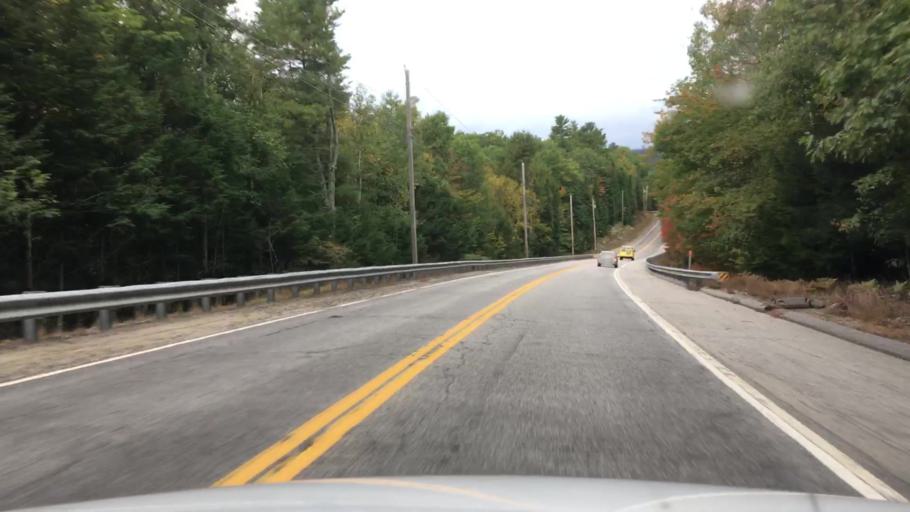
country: US
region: Maine
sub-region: Oxford County
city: Norway
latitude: 44.2197
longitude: -70.6077
